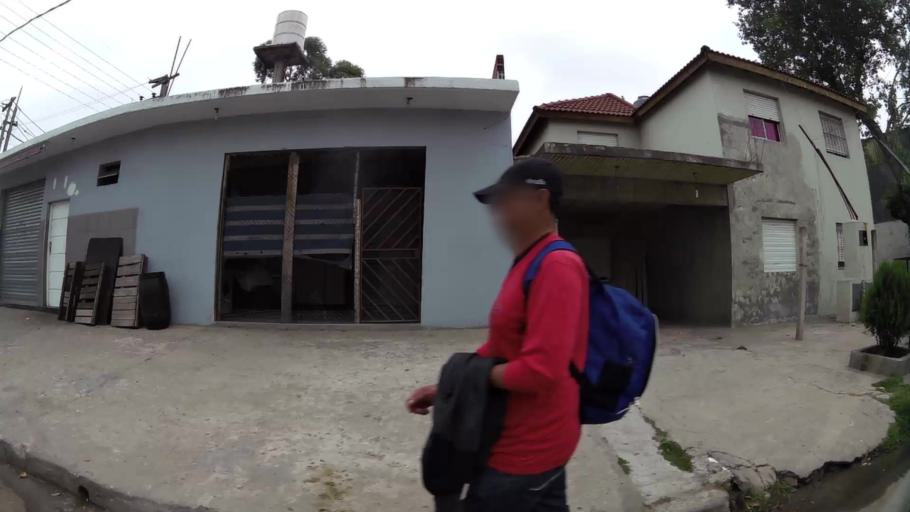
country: AR
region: Buenos Aires
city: San Justo
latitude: -34.6957
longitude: -58.5477
